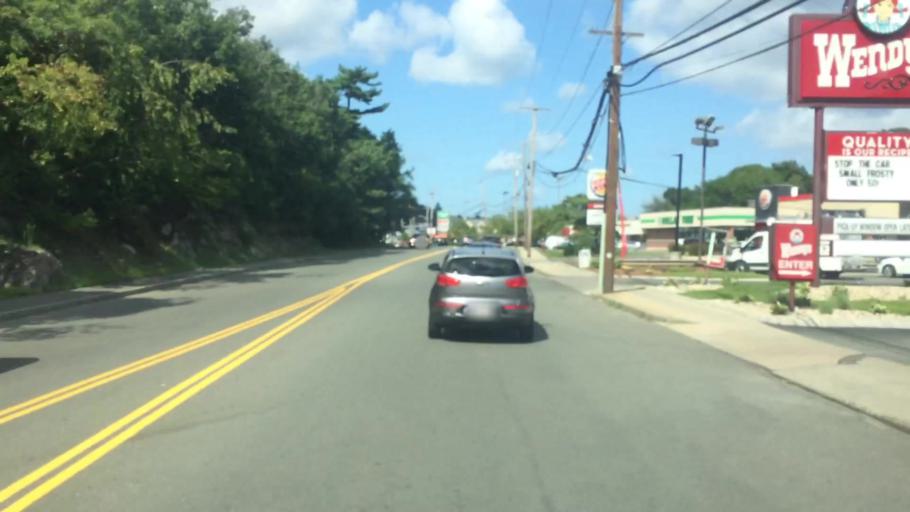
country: US
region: Massachusetts
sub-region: Essex County
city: Lynn
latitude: 42.4746
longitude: -70.9581
